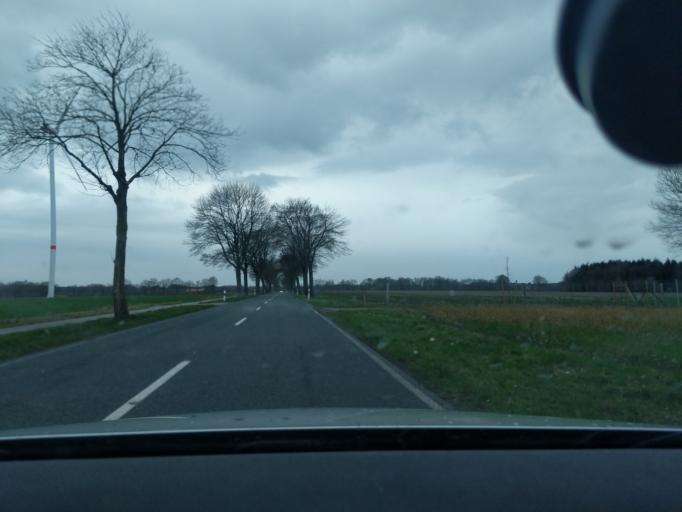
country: DE
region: Lower Saxony
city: Kutenholz
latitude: 53.4842
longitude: 9.2613
